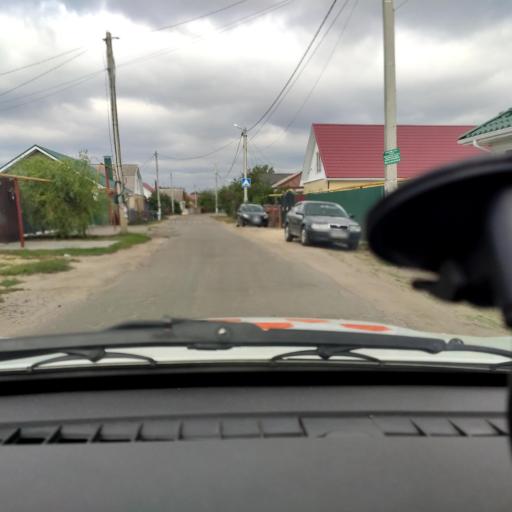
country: RU
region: Voronezj
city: Novaya Usman'
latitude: 51.6212
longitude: 39.4013
